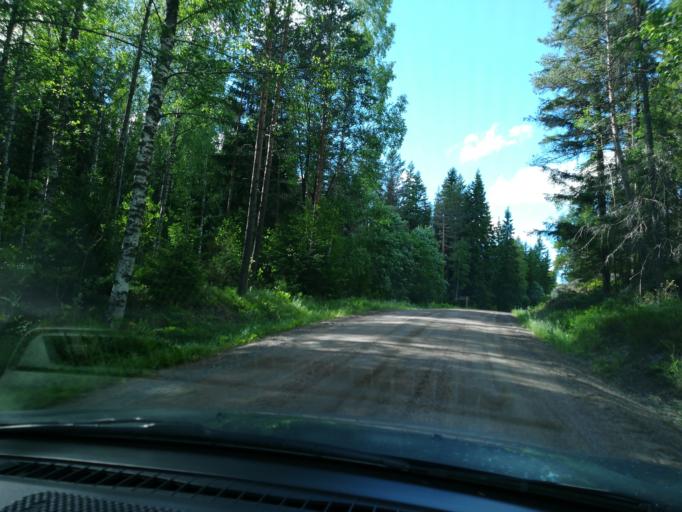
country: FI
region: South Karelia
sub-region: Lappeenranta
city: Savitaipale
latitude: 61.3046
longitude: 27.6371
